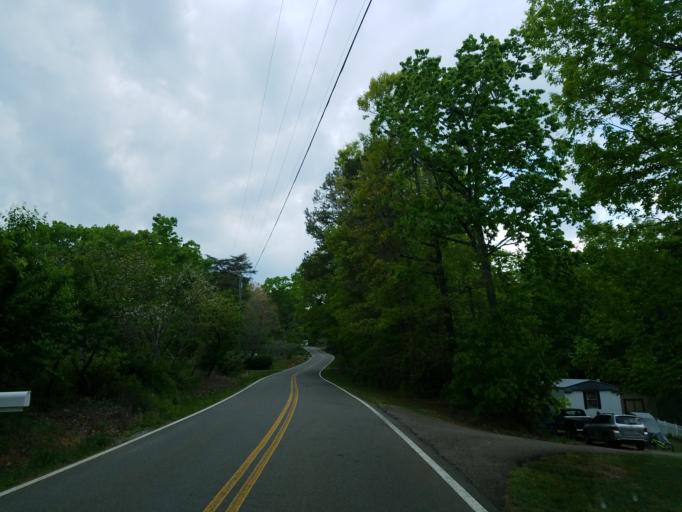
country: US
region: Georgia
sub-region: Pickens County
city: Jasper
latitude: 34.4415
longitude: -84.4745
